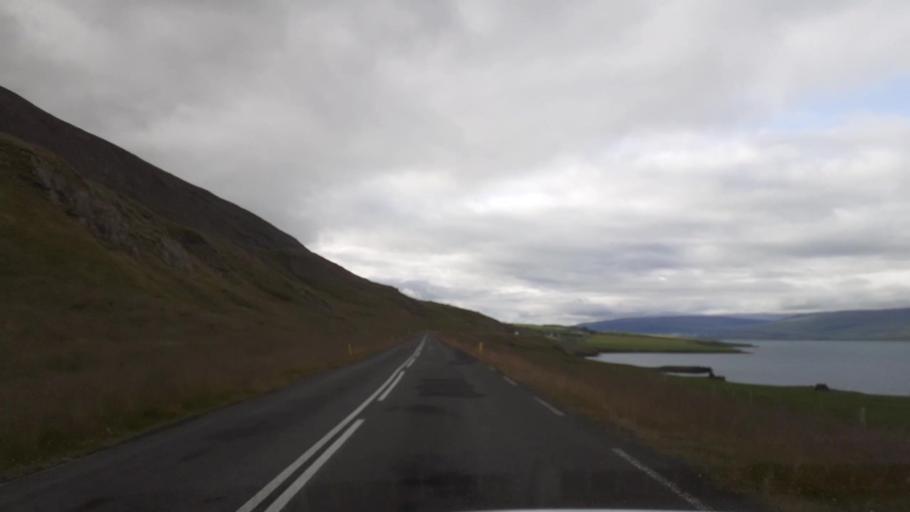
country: IS
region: Northeast
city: Akureyri
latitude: 65.8064
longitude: -18.0566
